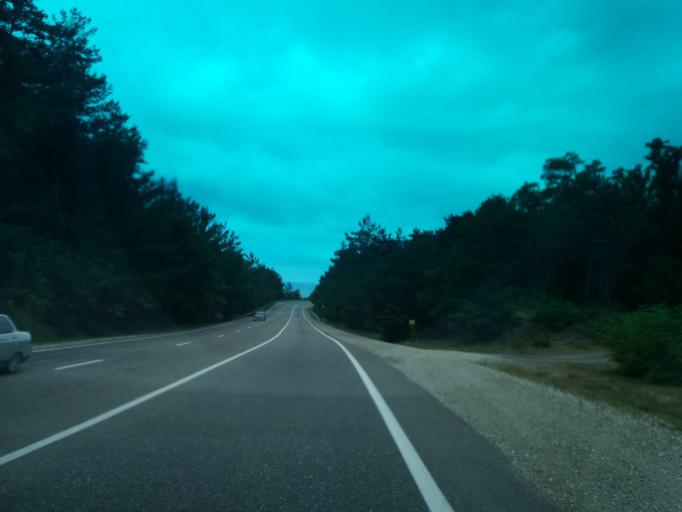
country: RU
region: Krasnodarskiy
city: Ol'ginka
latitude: 44.1825
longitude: 38.9322
